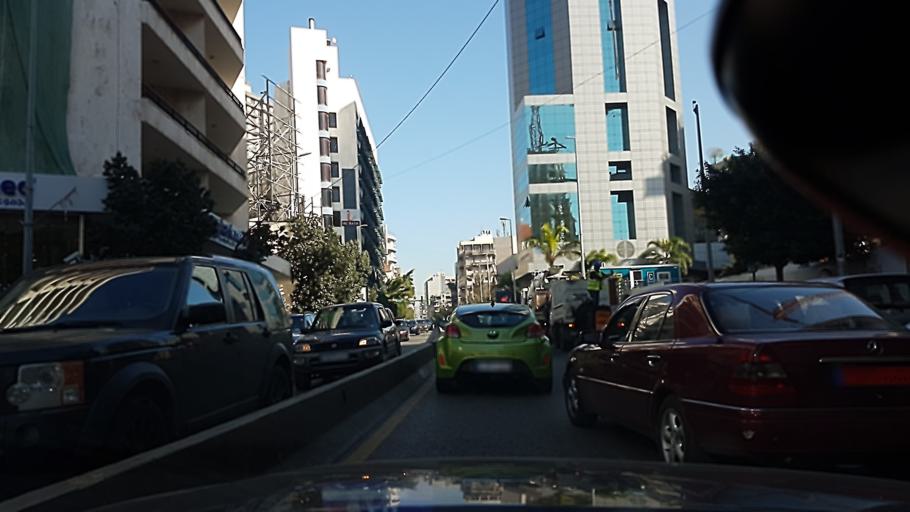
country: LB
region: Beyrouth
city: Beirut
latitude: 33.8921
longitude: 35.5142
